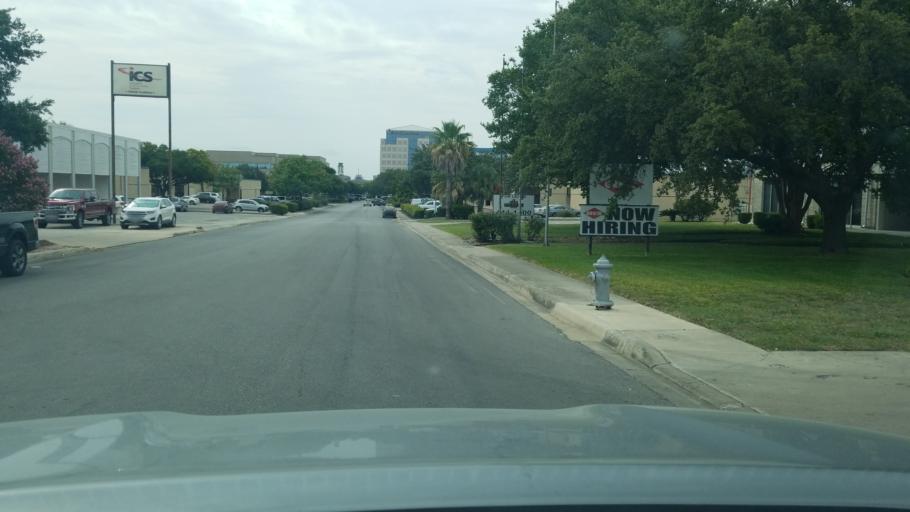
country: US
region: Texas
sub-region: Bexar County
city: Castle Hills
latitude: 29.5355
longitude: -98.4882
